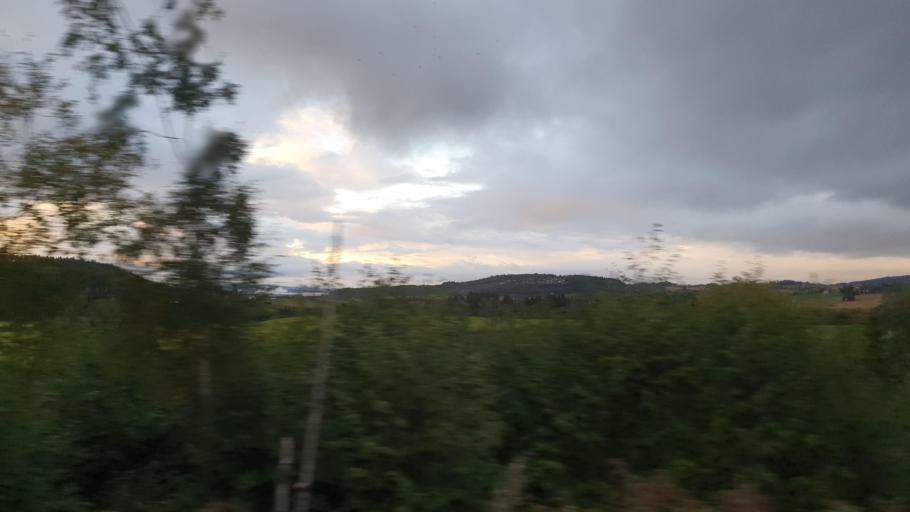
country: NO
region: Nord-Trondelag
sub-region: Levanger
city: Skogn
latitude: 63.6774
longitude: 11.1407
